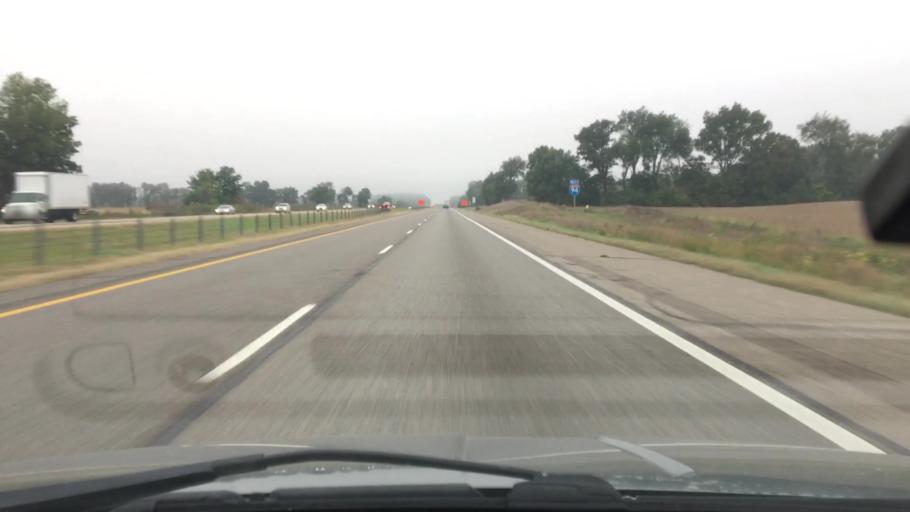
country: US
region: Michigan
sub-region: Calhoun County
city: Albion
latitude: 42.2839
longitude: -84.8085
